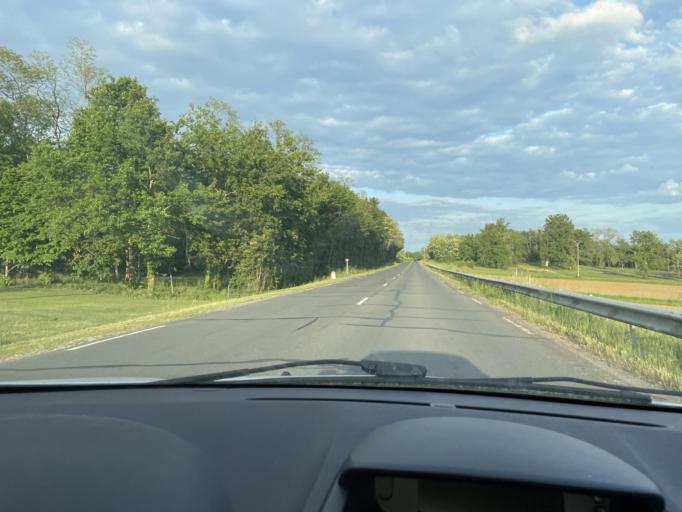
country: FR
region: Aquitaine
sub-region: Departement du Lot-et-Garonne
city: Casteljaloux
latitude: 44.3504
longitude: 0.0228
